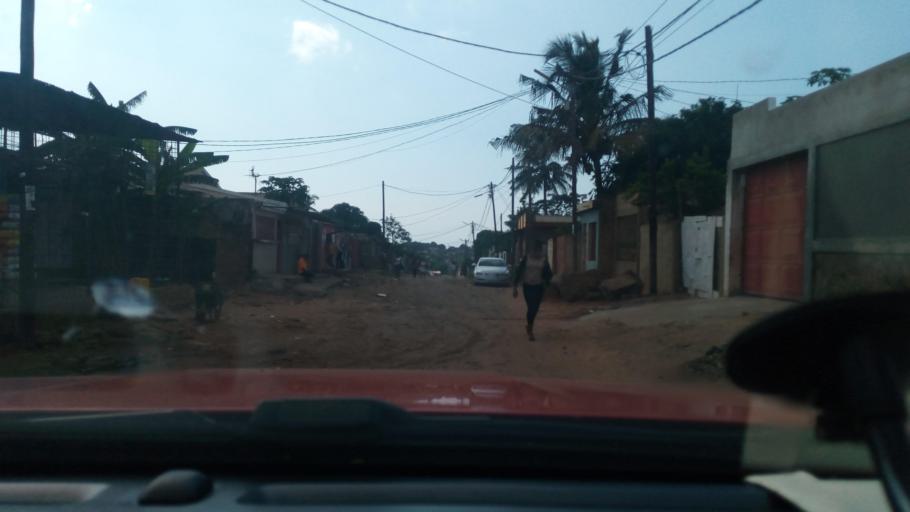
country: MZ
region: Maputo City
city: Maputo
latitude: -25.9197
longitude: 32.6013
